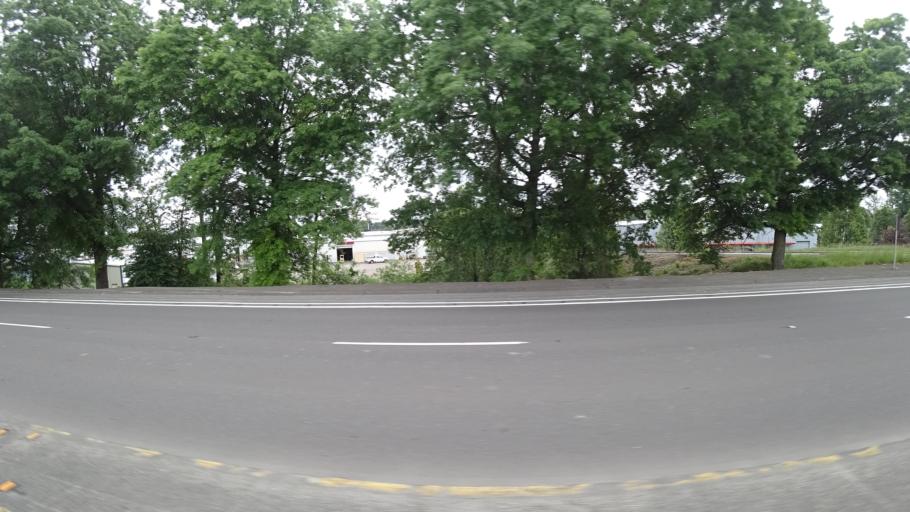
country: US
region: Washington
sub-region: Clark County
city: Vancouver
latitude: 45.5936
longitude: -122.6682
